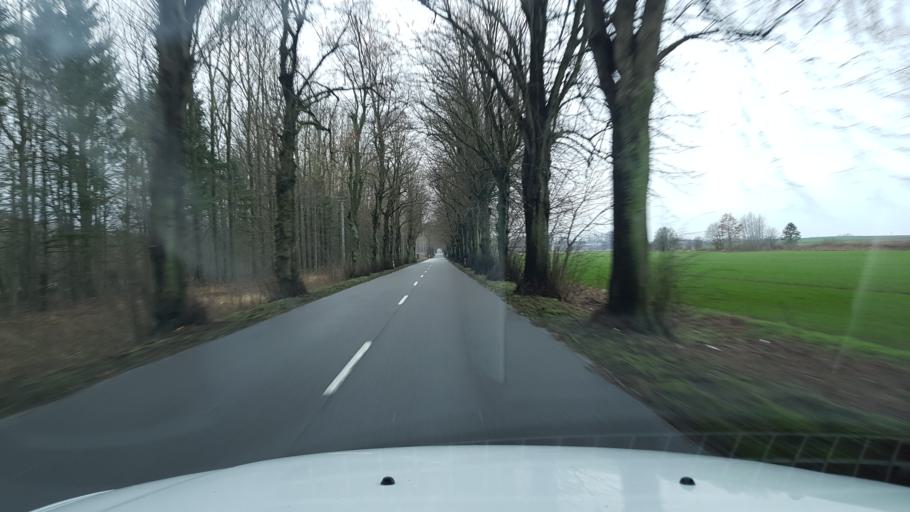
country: PL
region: West Pomeranian Voivodeship
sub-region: Powiat gryficki
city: Trzebiatow
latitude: 54.0593
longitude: 15.3171
